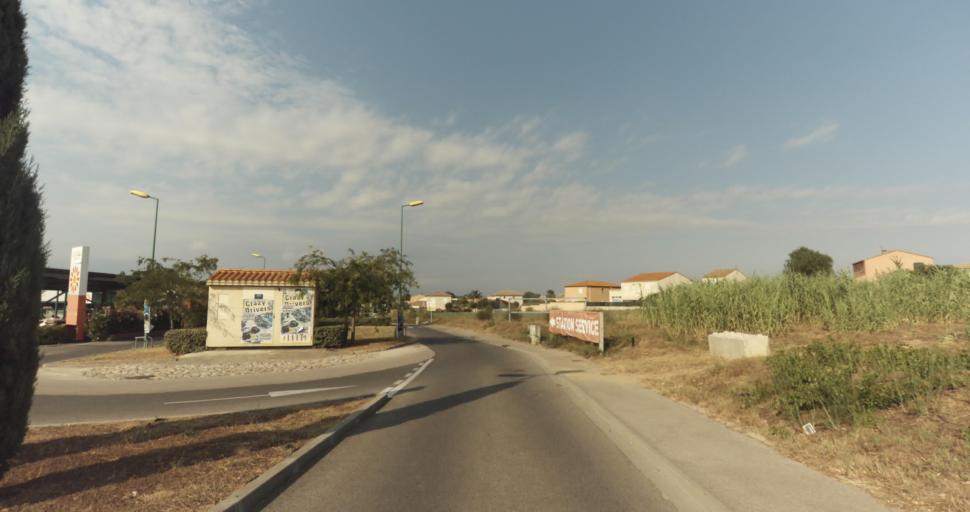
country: FR
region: Languedoc-Roussillon
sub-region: Departement des Pyrenees-Orientales
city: Latour-Bas-Elne
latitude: 42.6111
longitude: 3.0002
